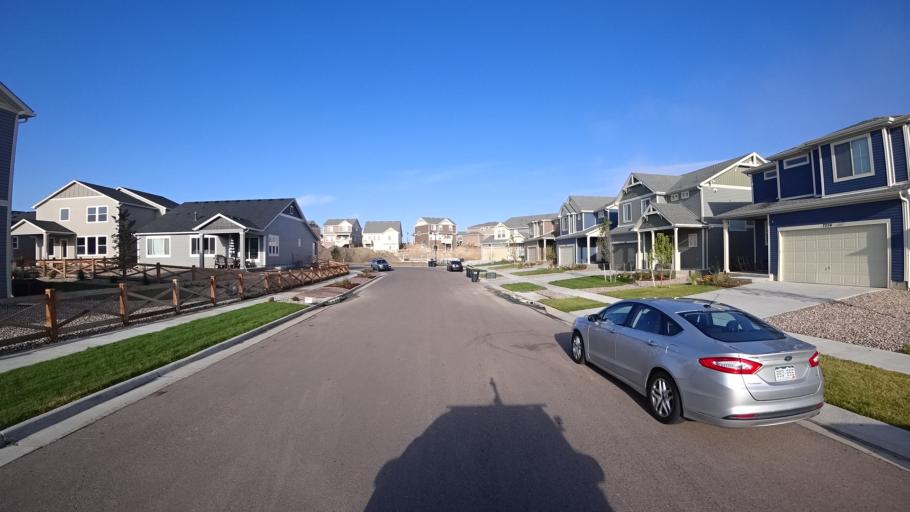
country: US
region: Colorado
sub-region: El Paso County
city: Cimarron Hills
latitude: 38.9359
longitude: -104.6554
